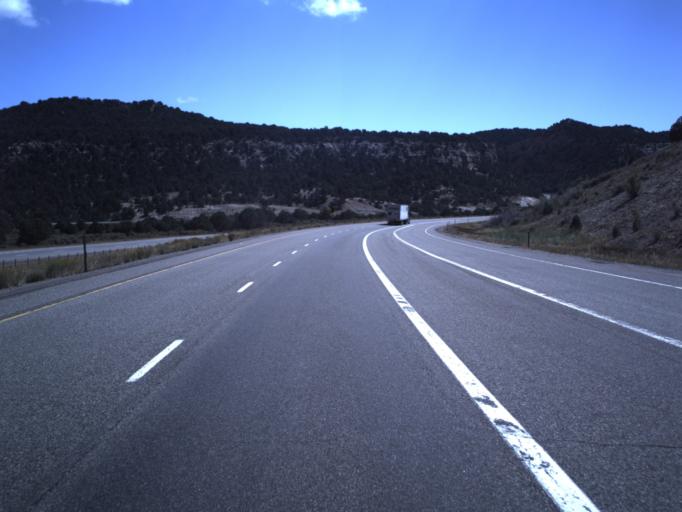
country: US
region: Utah
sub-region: Sevier County
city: Salina
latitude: 38.8773
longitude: -111.5595
